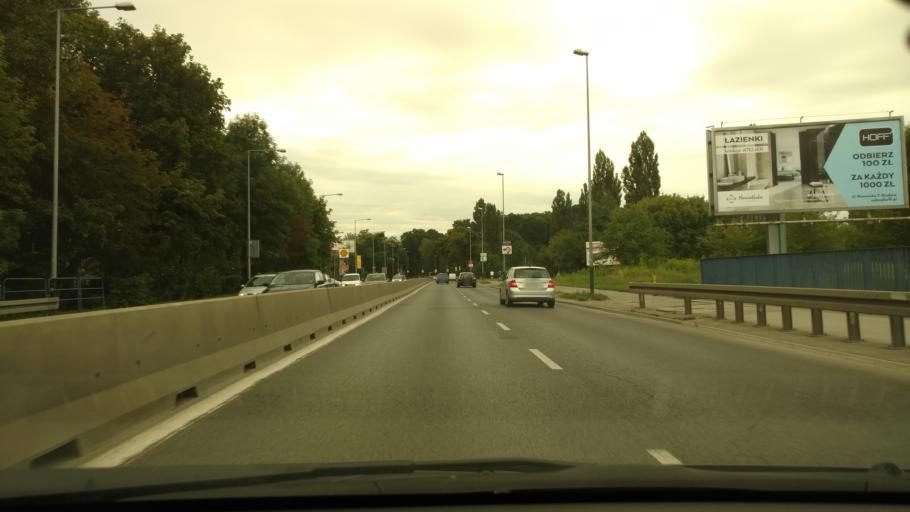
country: PL
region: Lesser Poland Voivodeship
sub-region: Krakow
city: Krakow
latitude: 50.0414
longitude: 19.9358
